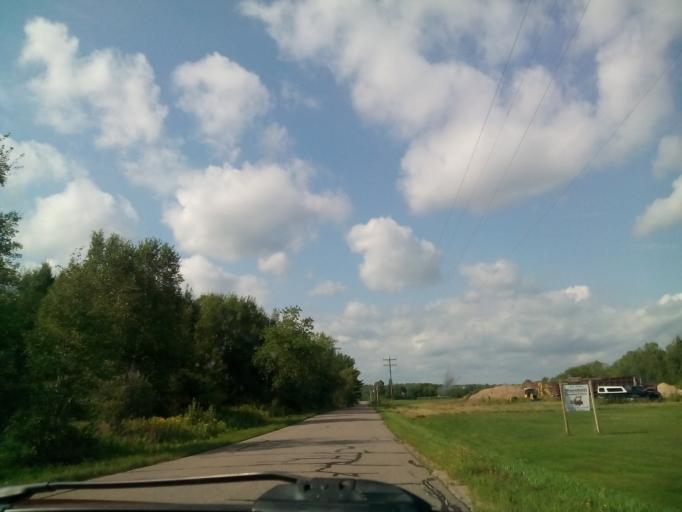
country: US
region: Wisconsin
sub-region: Menominee County
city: Legend Lake
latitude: 45.3088
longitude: -88.5220
